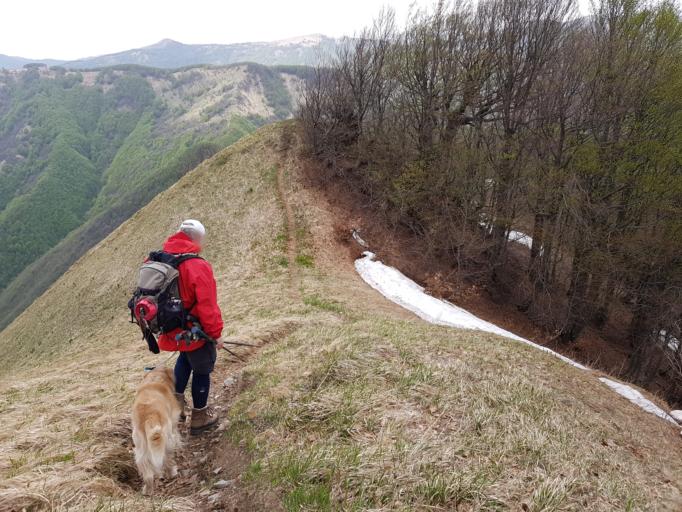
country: IT
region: Liguria
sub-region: Provincia di Genova
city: Gorreto
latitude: 44.6322
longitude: 9.2727
